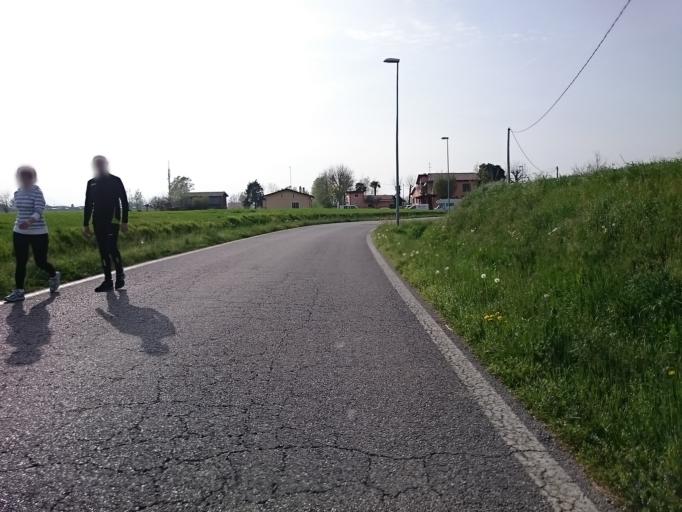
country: IT
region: Veneto
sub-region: Provincia di Padova
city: Bertipaglia
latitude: 45.3200
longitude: 11.8805
